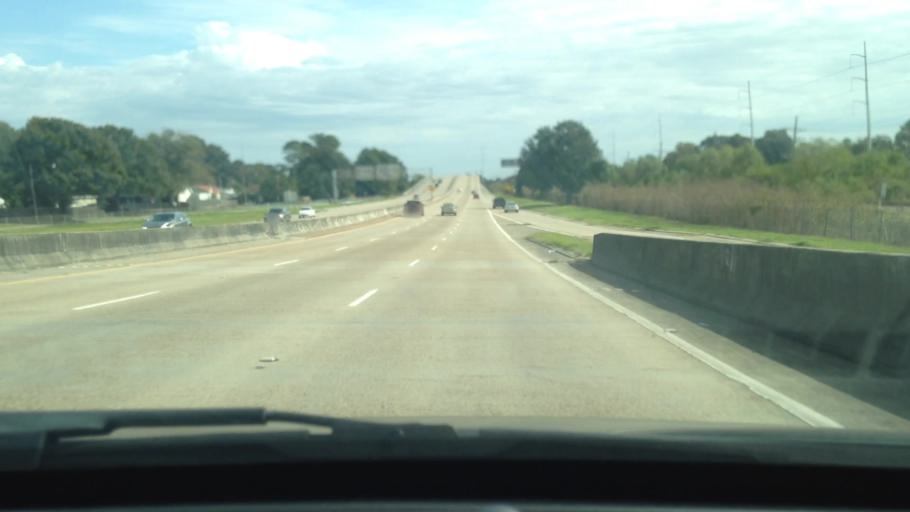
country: US
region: Louisiana
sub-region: Jefferson Parish
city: Metairie Terrace
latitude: 29.9714
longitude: -90.1696
